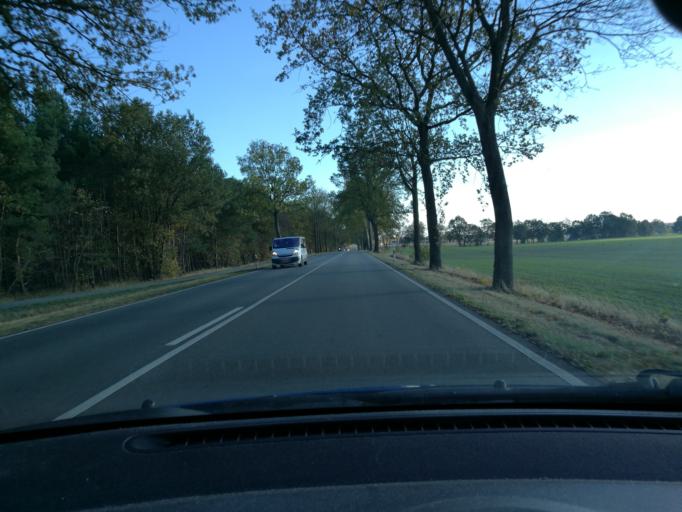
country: DE
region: Brandenburg
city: Perleberg
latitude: 53.1101
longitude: 11.8215
